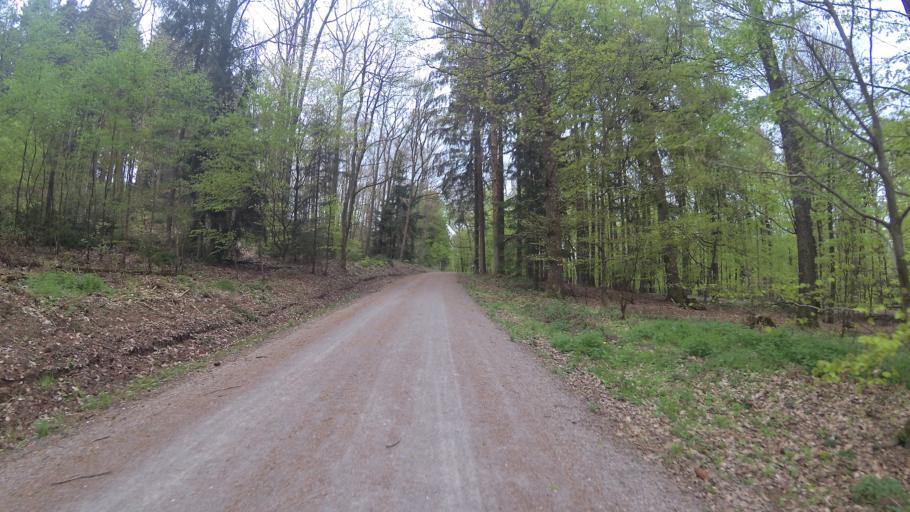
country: DE
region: Saarland
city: Mainzweiler
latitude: 49.3990
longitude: 7.1252
